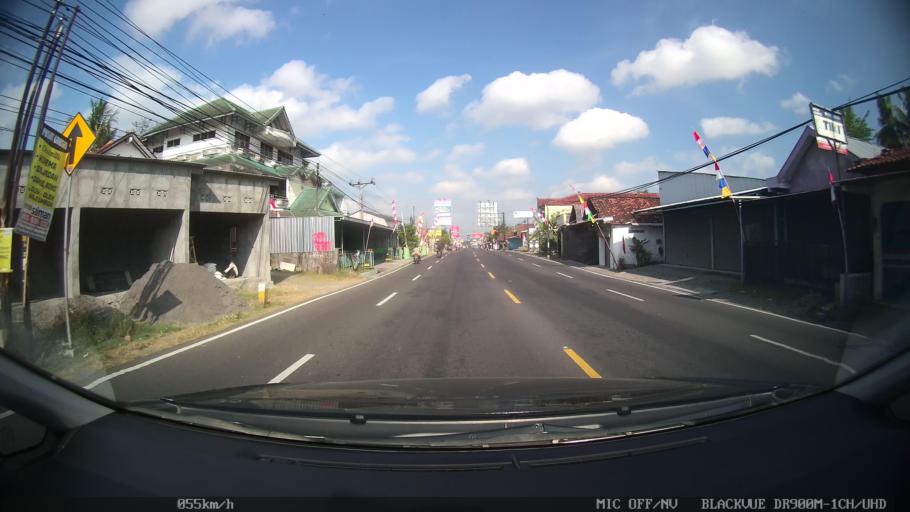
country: ID
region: Daerah Istimewa Yogyakarta
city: Godean
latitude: -7.8117
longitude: 110.2734
